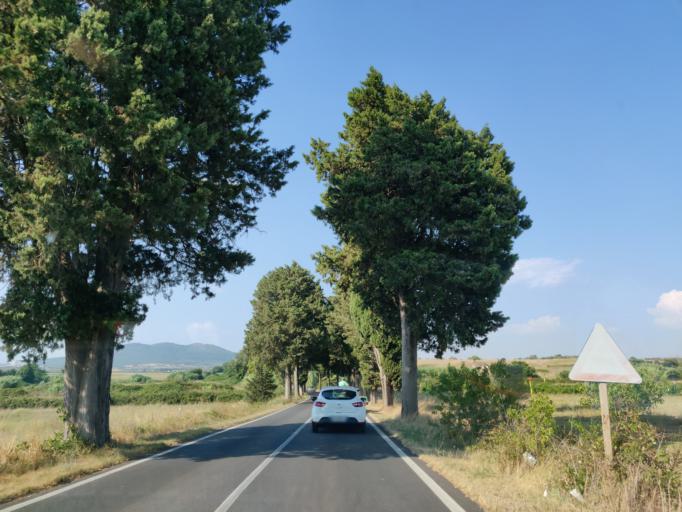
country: IT
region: Latium
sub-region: Provincia di Viterbo
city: Canino
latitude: 42.4051
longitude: 11.6947
